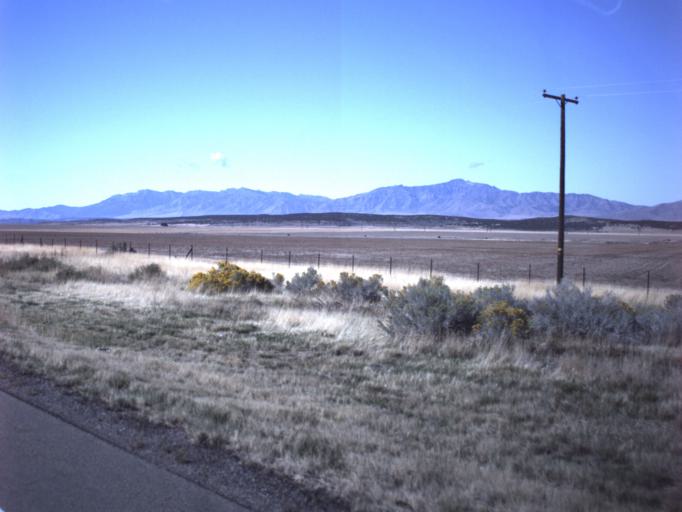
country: US
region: Utah
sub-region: Juab County
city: Nephi
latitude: 39.4668
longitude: -111.8988
